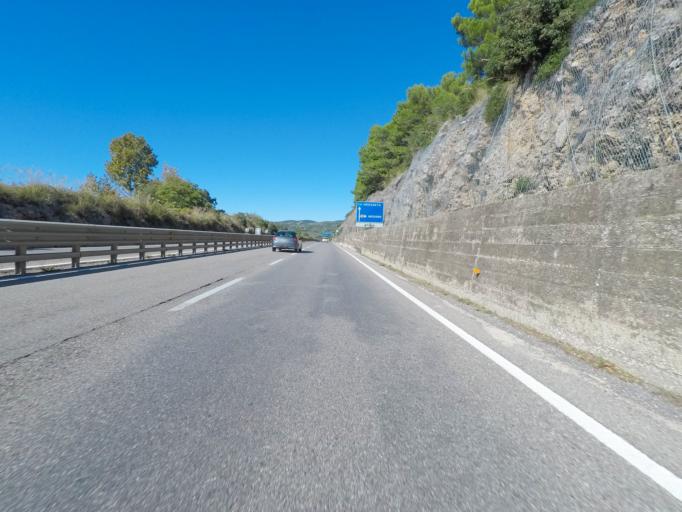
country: IT
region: Tuscany
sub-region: Provincia di Grosseto
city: Orbetello Scalo
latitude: 42.4243
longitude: 11.2882
